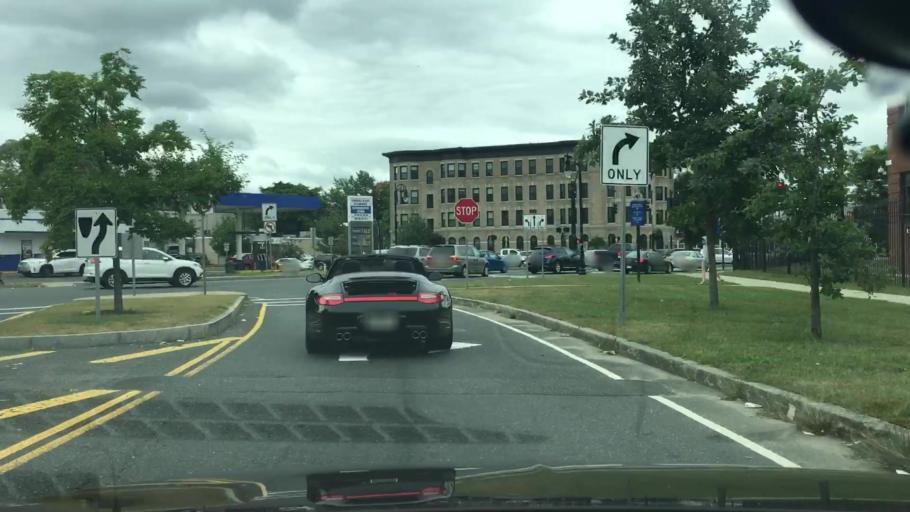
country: US
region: Massachusetts
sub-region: Hampden County
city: Springfield
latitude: 42.1100
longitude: -72.5747
